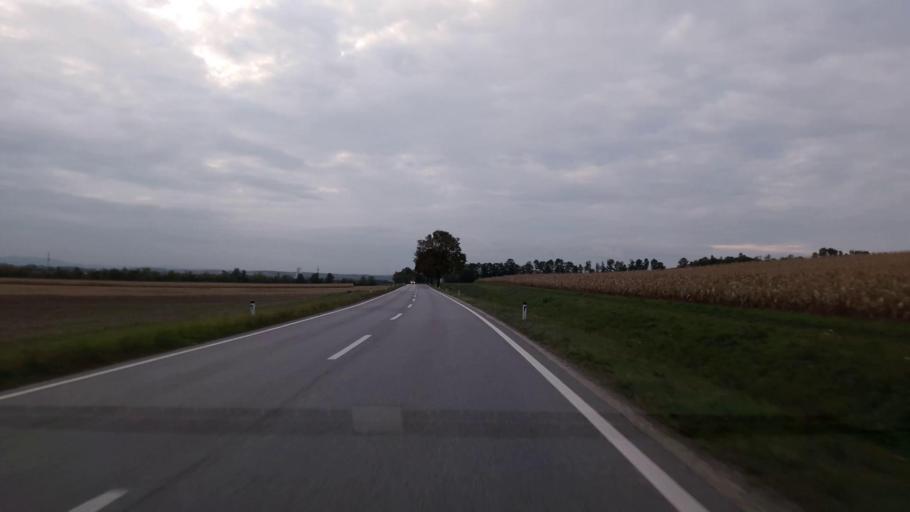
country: AT
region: Lower Austria
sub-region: Politischer Bezirk Bruck an der Leitha
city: Enzersdorf an der Fischa
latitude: 48.0588
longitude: 16.6281
